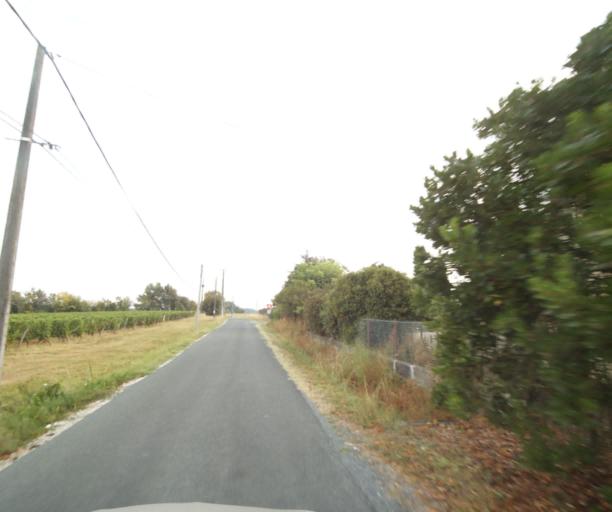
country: FR
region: Aquitaine
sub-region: Departement de la Gironde
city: Creon
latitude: 44.7775
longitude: -0.3395
